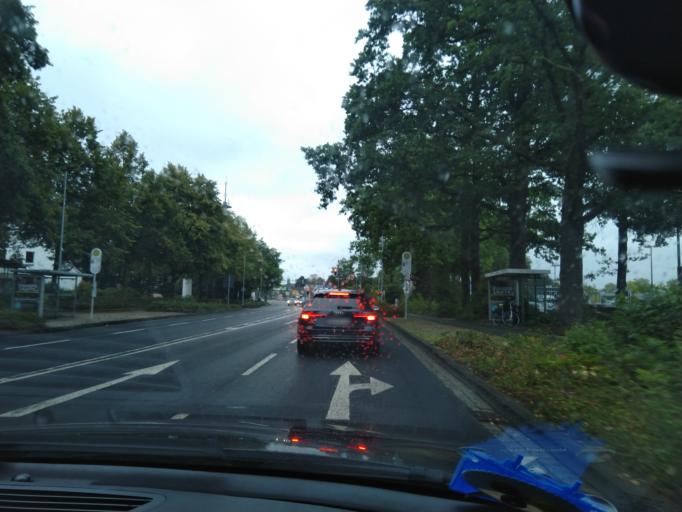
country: DE
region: Lower Saxony
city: Nordhorn
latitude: 52.4276
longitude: 7.0610
